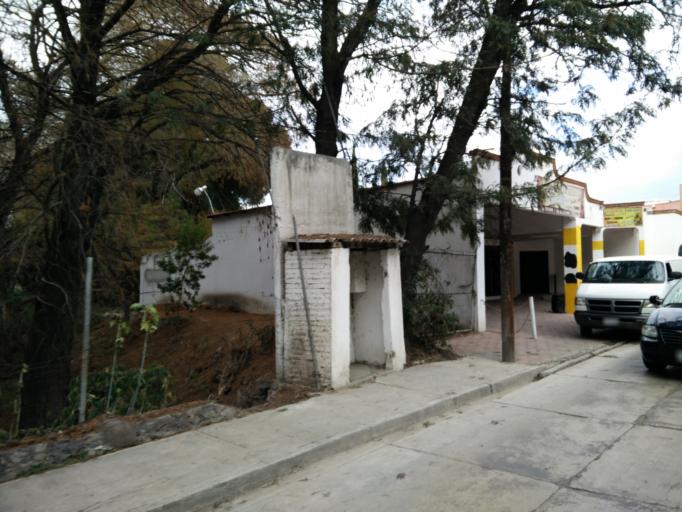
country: MX
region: Queretaro
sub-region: Tequisquiapan
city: Tequisquiapan
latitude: 20.5266
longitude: -99.8913
